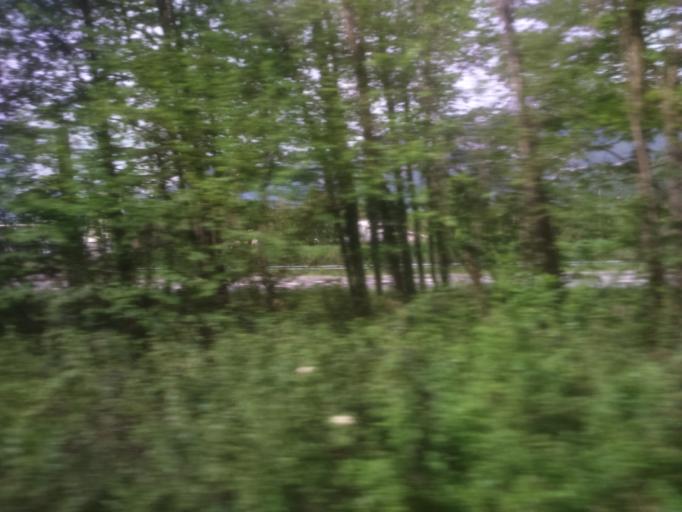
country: FR
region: Rhone-Alpes
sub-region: Departement de l'Isere
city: Le Pont-de-Claix
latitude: 45.1101
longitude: 5.7093
